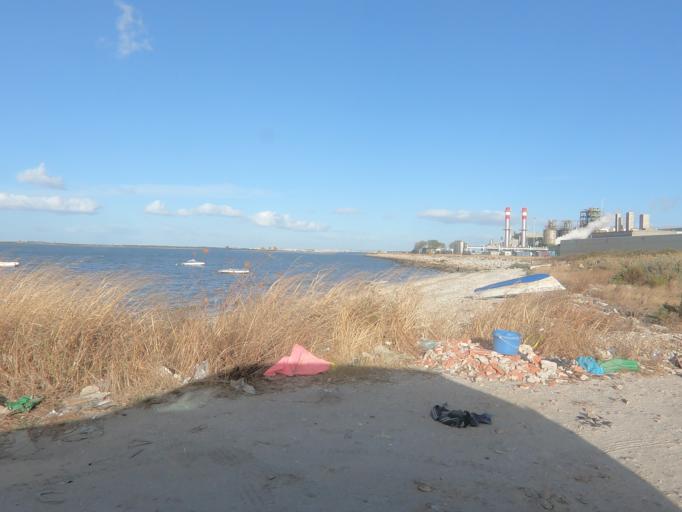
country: PT
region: Setubal
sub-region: Barreiro
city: Barreiro
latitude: 38.6776
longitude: -9.0545
